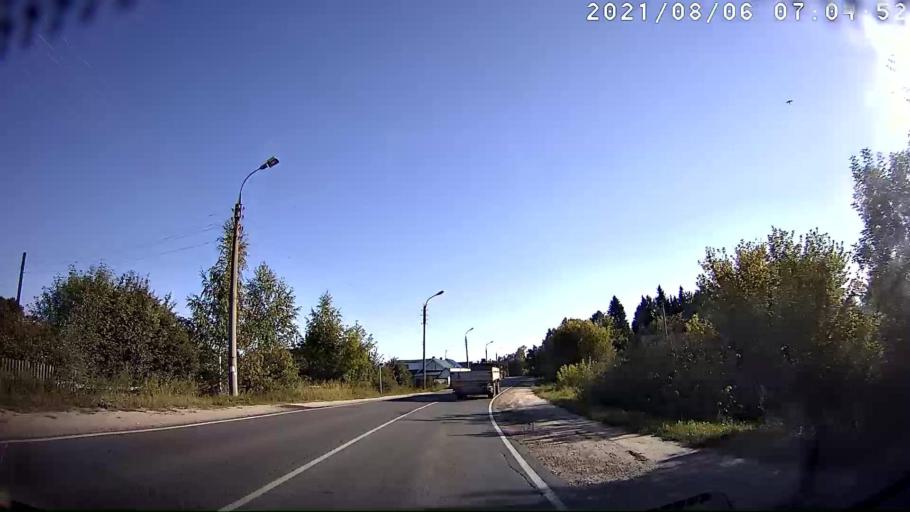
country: RU
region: Mariy-El
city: Yoshkar-Ola
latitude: 56.5501
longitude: 47.9839
